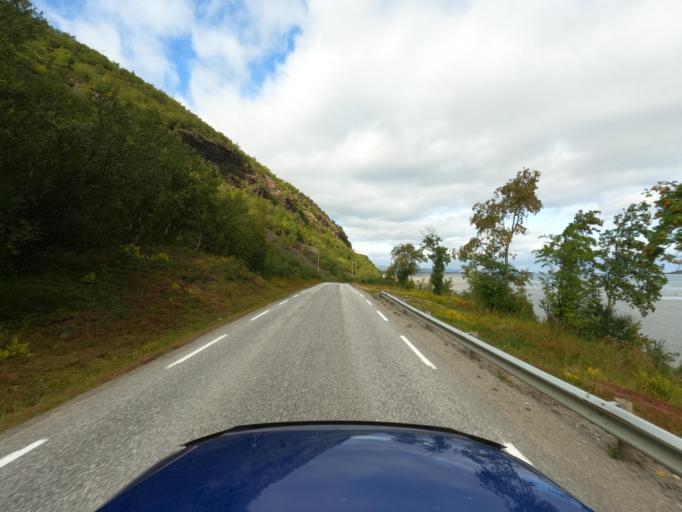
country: NO
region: Finnmark Fylke
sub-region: Porsanger
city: Lakselv
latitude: 70.1253
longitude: 24.9162
